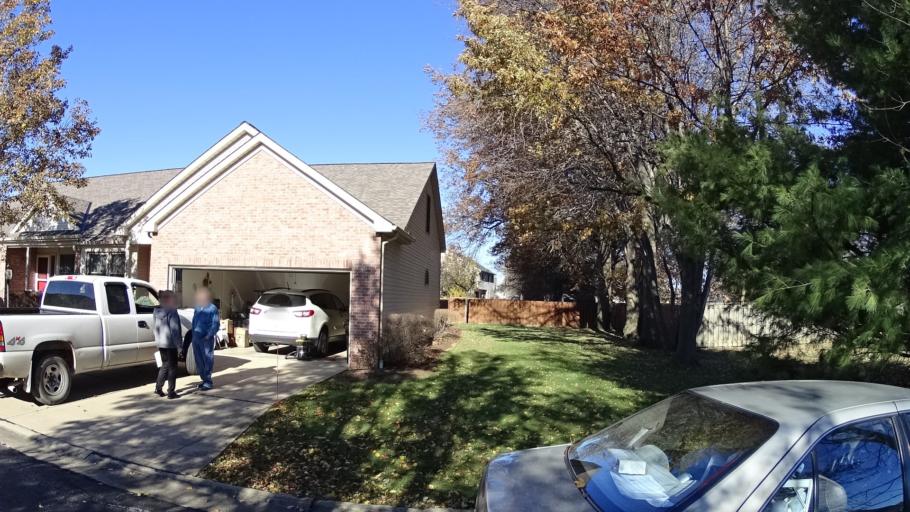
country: US
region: Ohio
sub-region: Lorain County
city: Elyria
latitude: 41.3452
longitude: -82.0823
